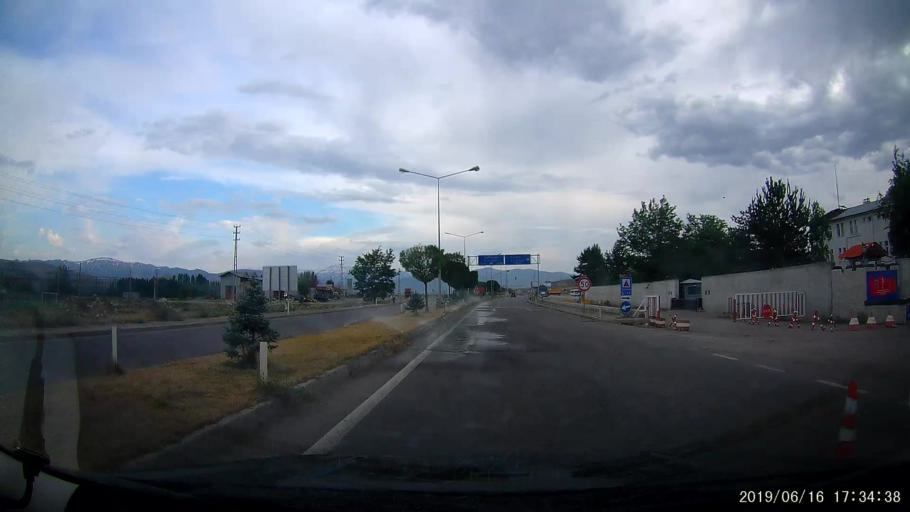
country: TR
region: Erzincan
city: Tercan
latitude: 39.7401
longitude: 40.2674
